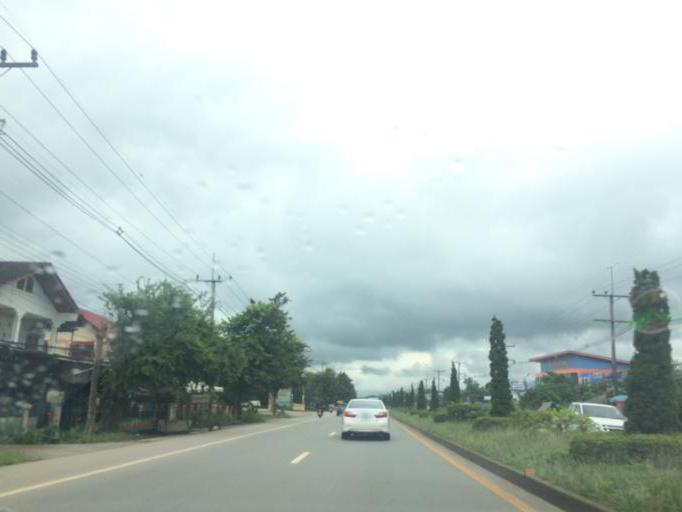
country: TH
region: Chiang Rai
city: Chiang Rai
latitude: 20.0242
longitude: 99.8719
